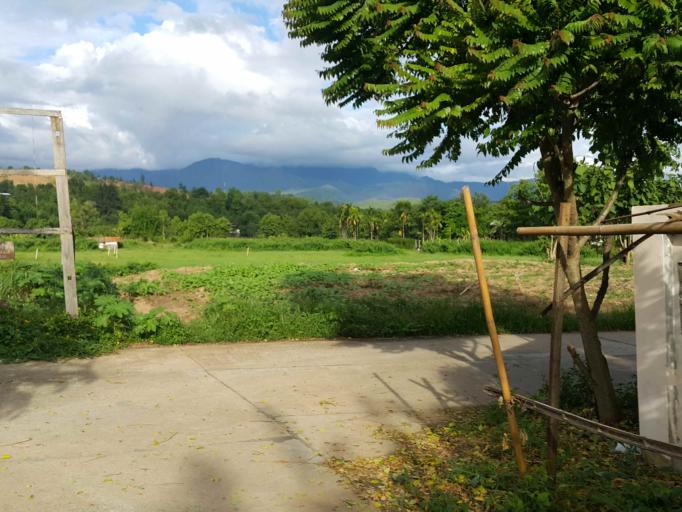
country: TH
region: Chiang Mai
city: Mae Chaem
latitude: 18.5020
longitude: 98.3633
